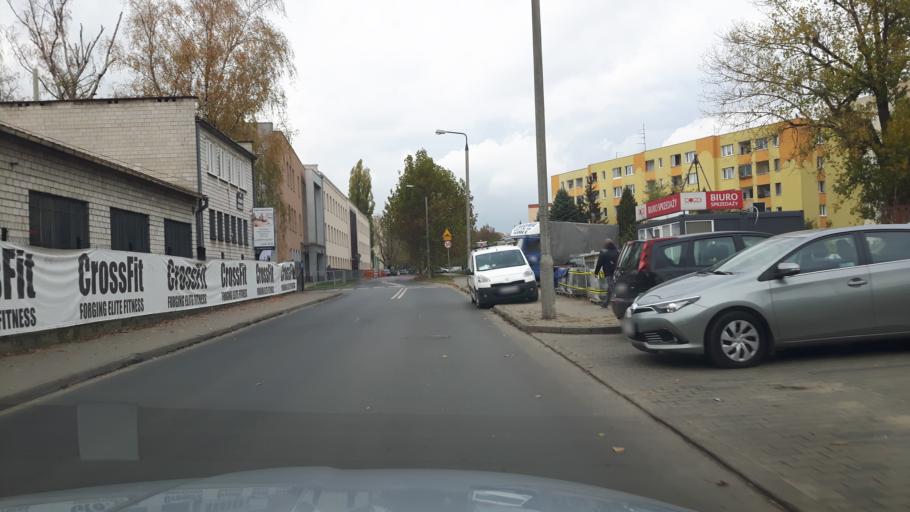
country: PL
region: Masovian Voivodeship
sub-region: Warszawa
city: Praga Polnoc
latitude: 52.2681
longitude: 21.0433
